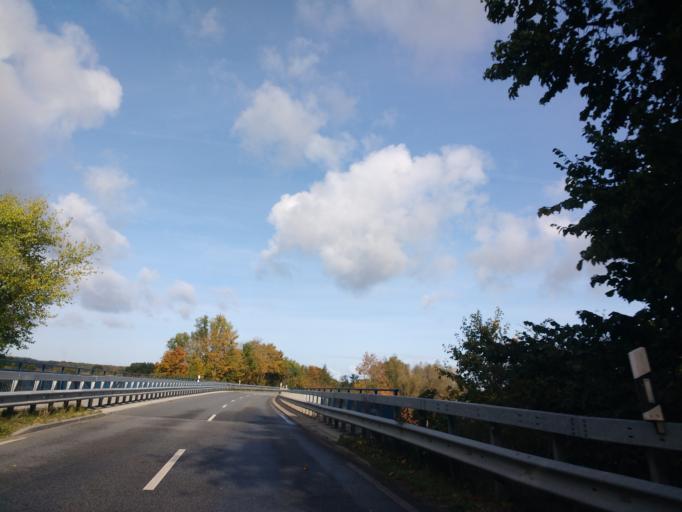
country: DE
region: Schleswig-Holstein
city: Altenkrempe
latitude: 54.1258
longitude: 10.8221
